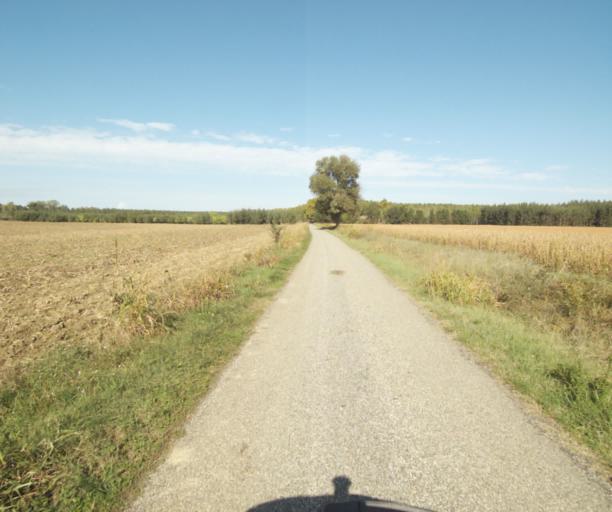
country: FR
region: Midi-Pyrenees
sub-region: Departement du Tarn-et-Garonne
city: Finhan
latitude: 43.8979
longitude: 1.2192
